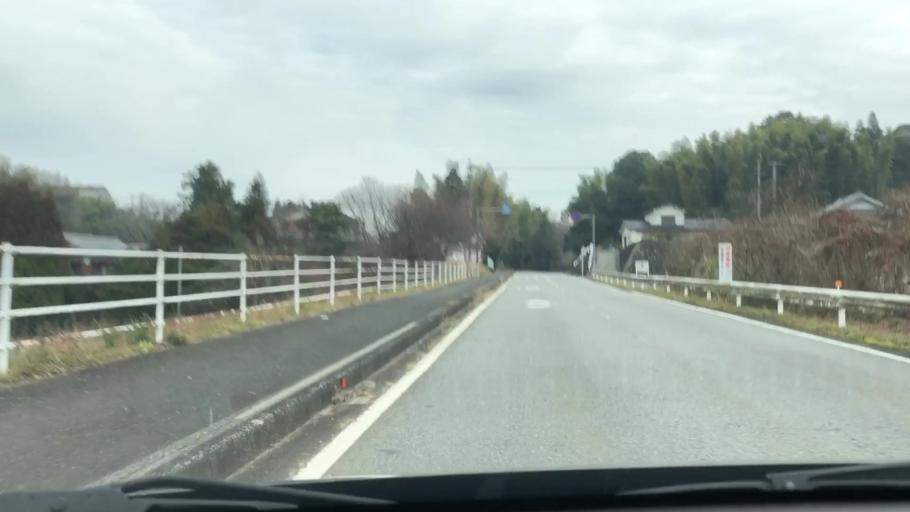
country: JP
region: Oita
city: Usuki
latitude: 33.0149
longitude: 131.6666
